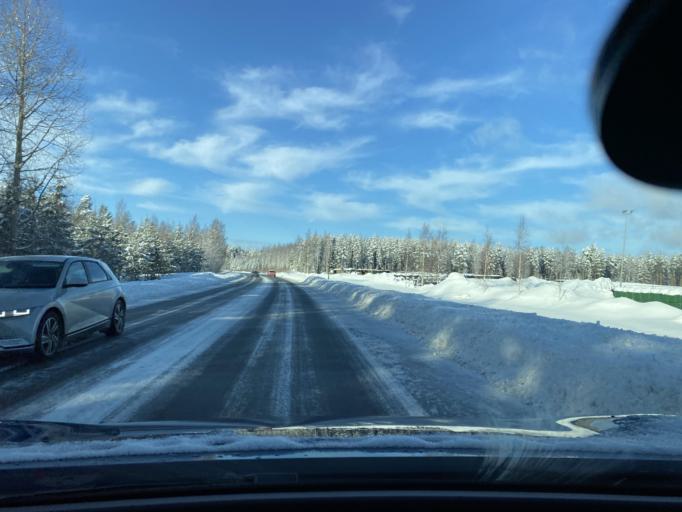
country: FI
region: Southern Savonia
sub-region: Mikkeli
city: Kangasniemi
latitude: 62.0097
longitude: 26.6378
